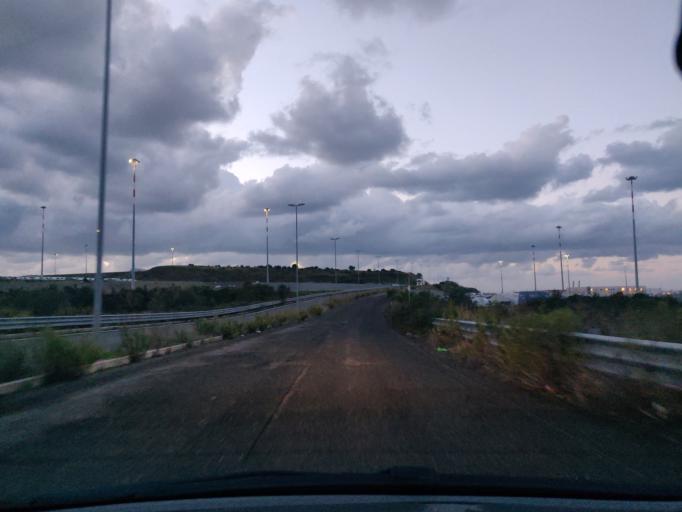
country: IT
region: Latium
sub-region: Citta metropolitana di Roma Capitale
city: Aurelia
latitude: 42.1297
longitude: 11.7778
